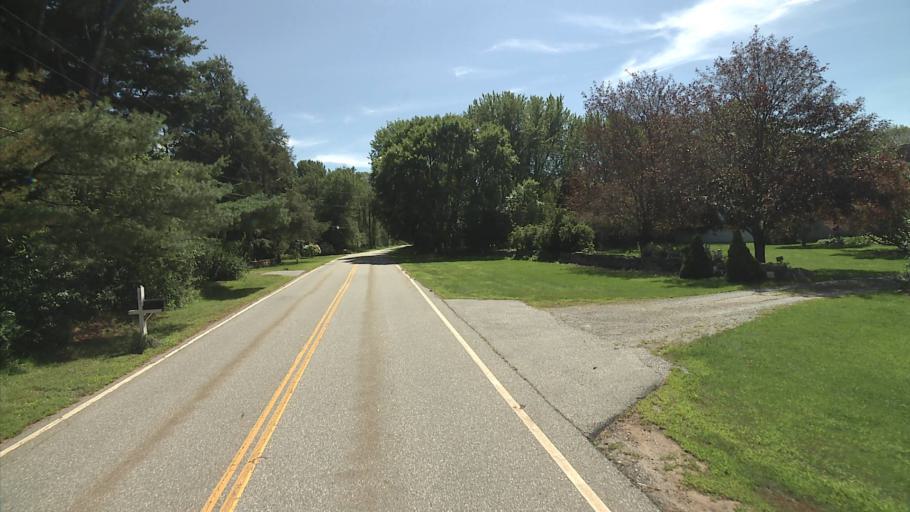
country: US
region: Connecticut
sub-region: Windham County
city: Windham
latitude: 41.7261
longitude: -72.0681
